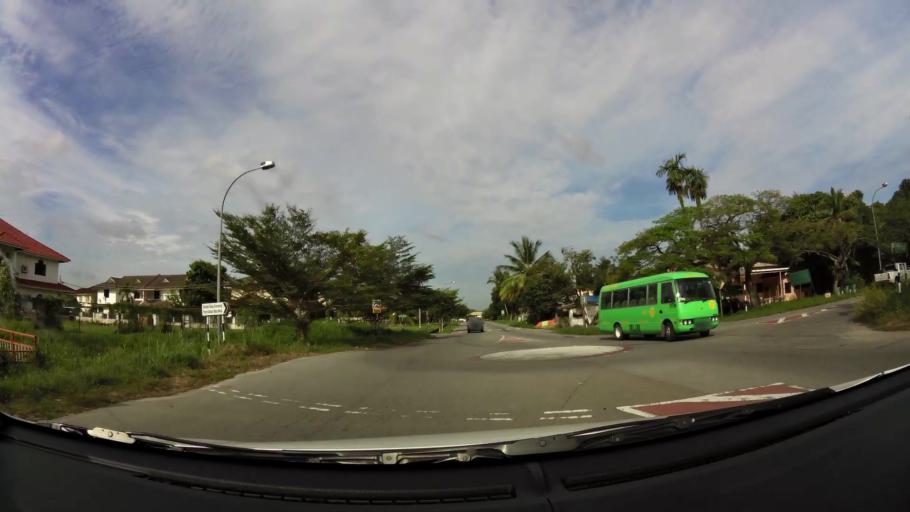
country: BN
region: Brunei and Muara
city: Bandar Seri Begawan
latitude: 4.9015
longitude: 114.8884
